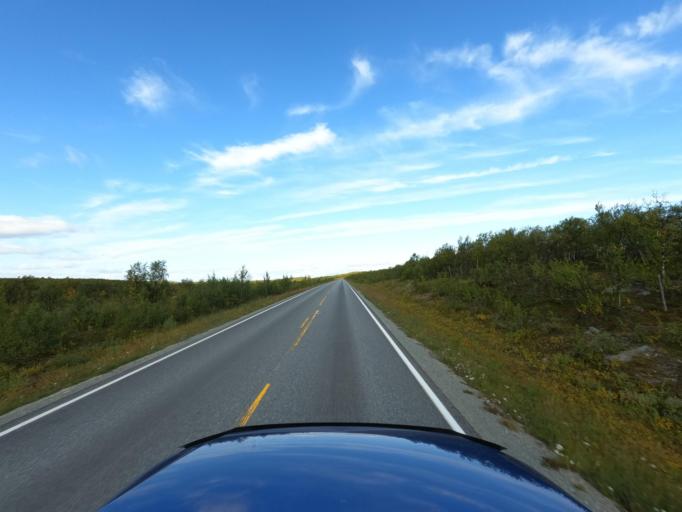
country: NO
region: Finnmark Fylke
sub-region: Karasjok
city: Karasjohka
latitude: 69.6952
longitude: 25.2576
